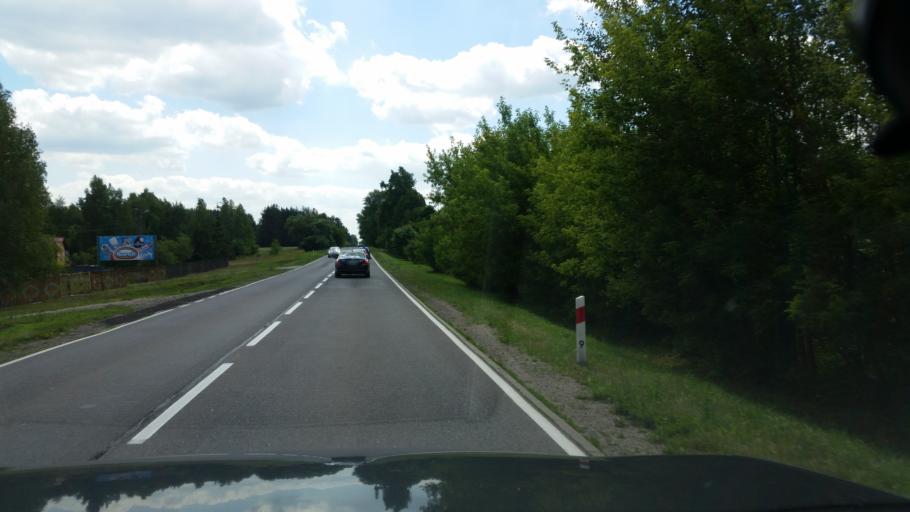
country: PL
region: Masovian Voivodeship
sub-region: Powiat ostrowski
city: Ostrow Mazowiecka
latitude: 52.8572
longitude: 21.8674
